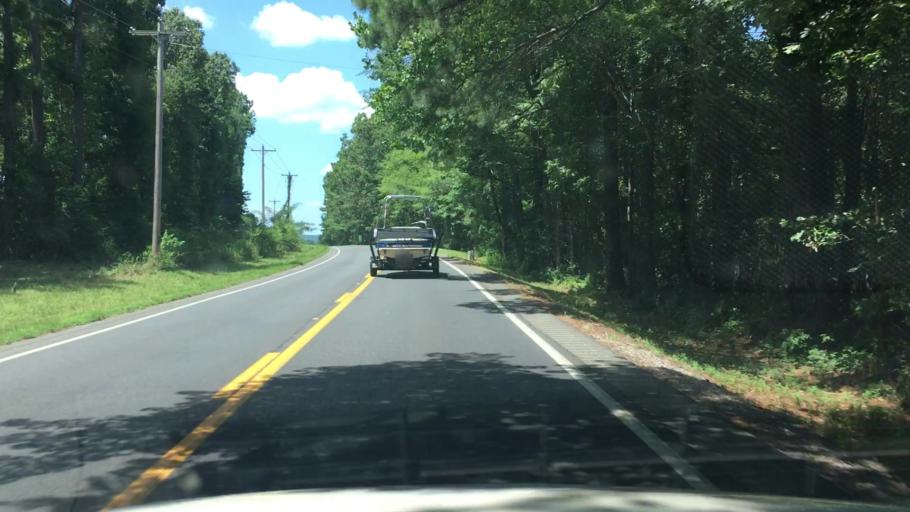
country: US
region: Arkansas
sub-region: Garland County
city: Lake Hamilton
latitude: 34.3097
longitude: -93.1680
